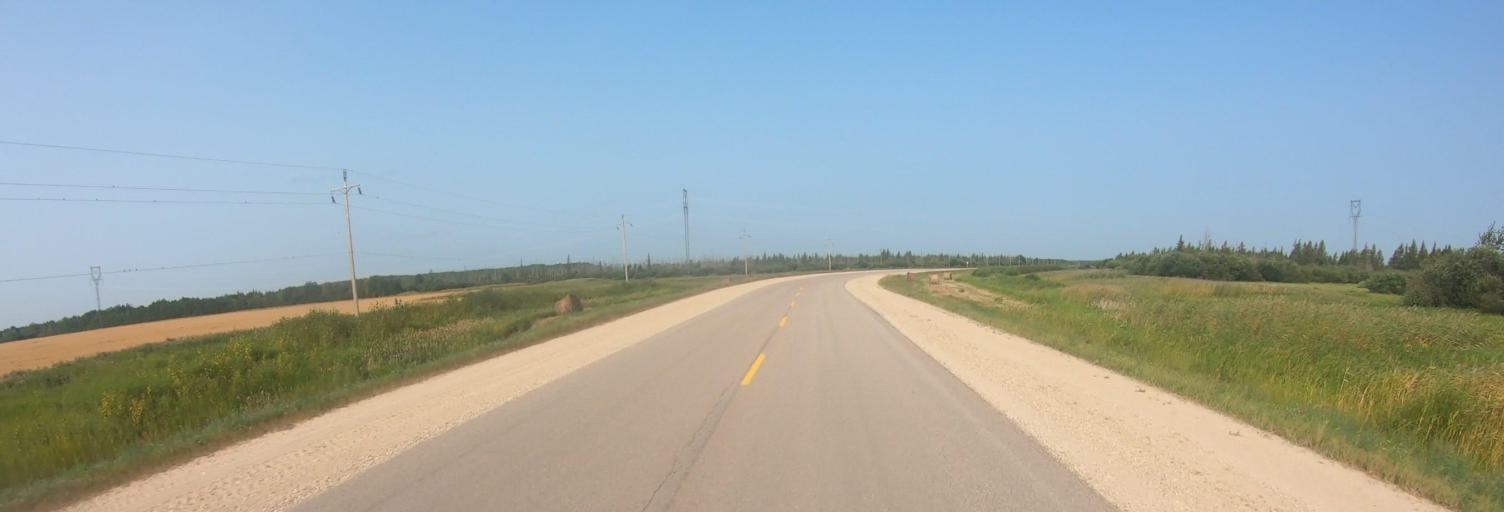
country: US
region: Minnesota
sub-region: Roseau County
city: Warroad
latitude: 49.0156
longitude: -95.5340
